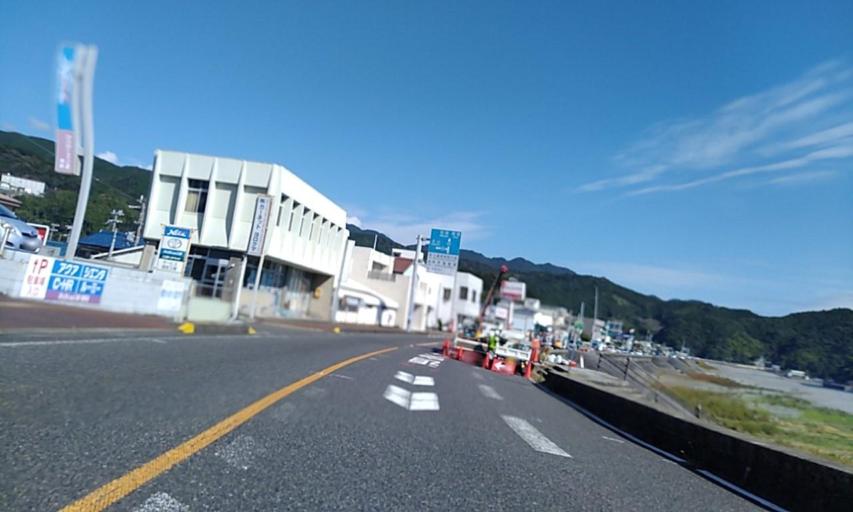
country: JP
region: Wakayama
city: Shingu
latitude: 33.8846
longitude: 136.0979
